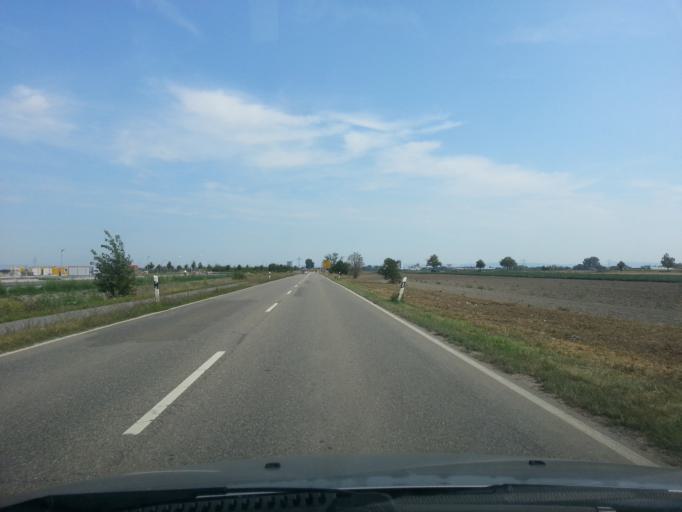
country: DE
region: Rheinland-Pfalz
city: Maxdorf
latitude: 49.4856
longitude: 8.3195
